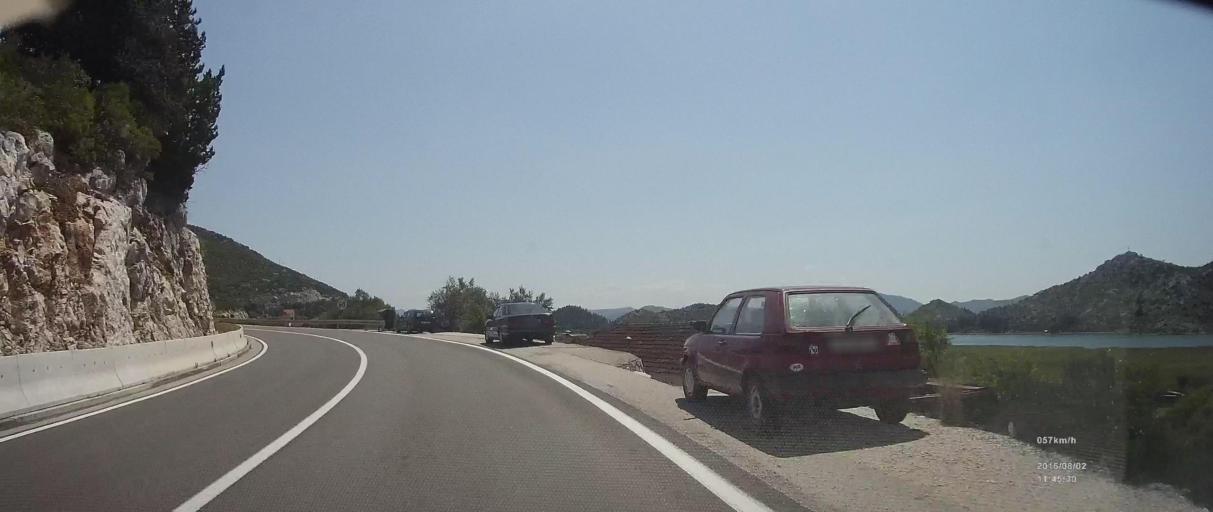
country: HR
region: Dubrovacko-Neretvanska
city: Komin
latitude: 43.0541
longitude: 17.4656
